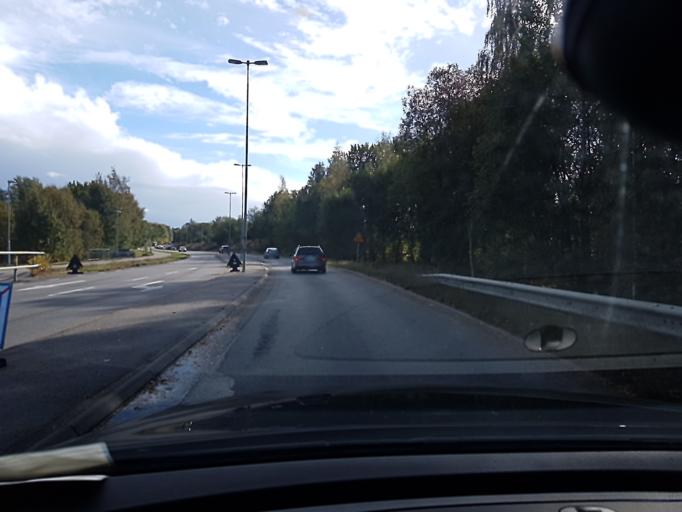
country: SE
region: Kronoberg
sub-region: Vaxjo Kommun
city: Vaexjoe
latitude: 56.8738
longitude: 14.7859
